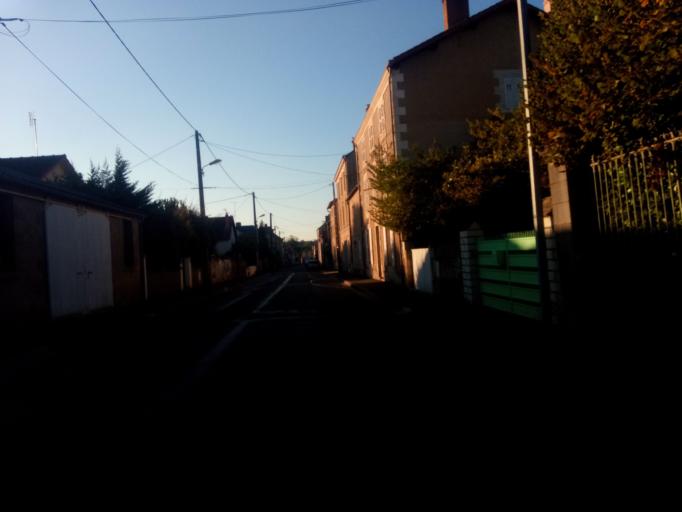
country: FR
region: Poitou-Charentes
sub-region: Departement de la Vienne
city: Montmorillon
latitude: 46.4194
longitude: 0.8719
